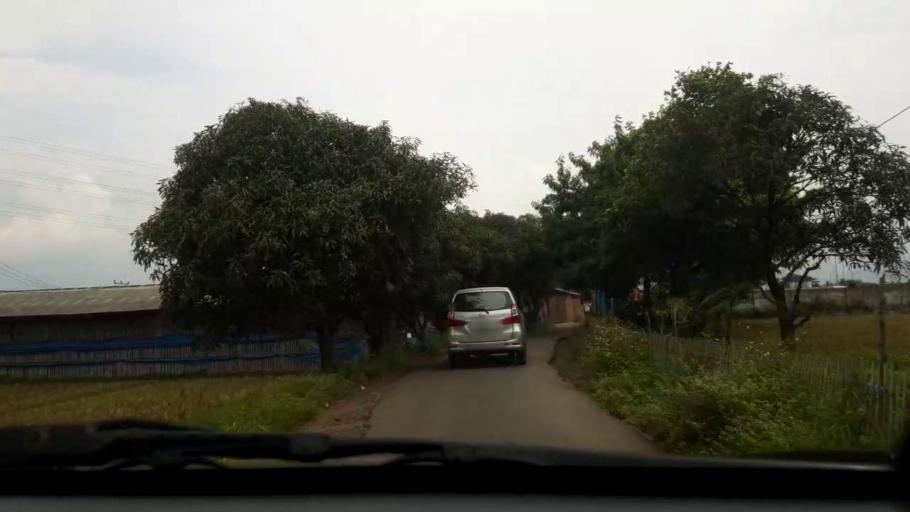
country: ID
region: West Java
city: Cileunyi
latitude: -6.9531
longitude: 107.7128
